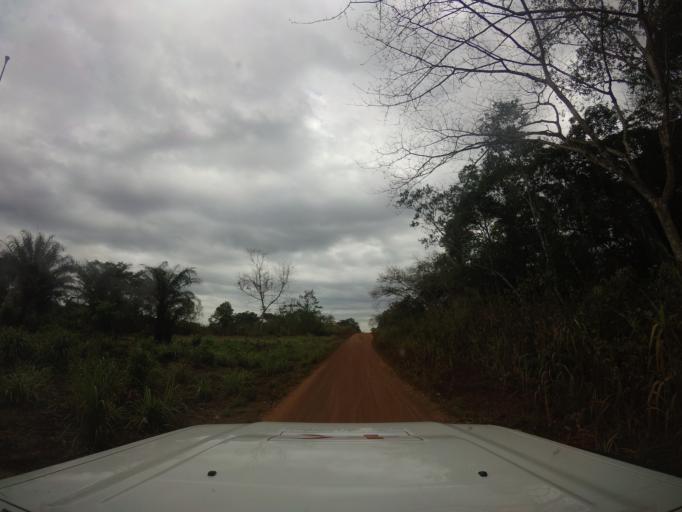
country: LR
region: Grand Cape Mount
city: Robertsport
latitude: 6.9375
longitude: -11.3302
